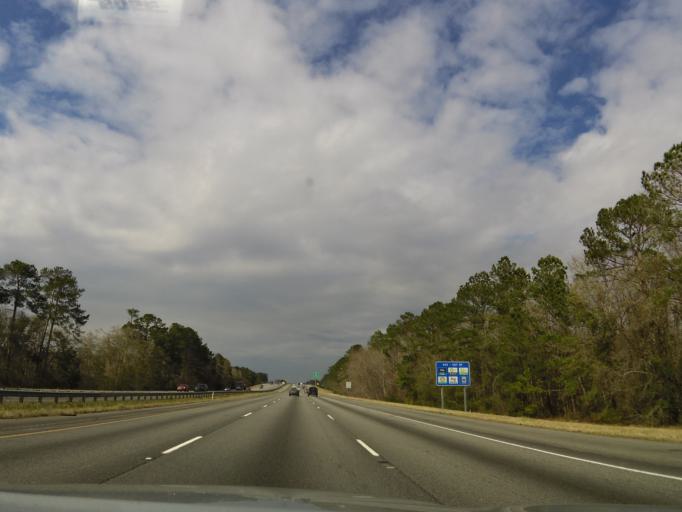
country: US
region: Georgia
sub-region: Bryan County
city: Richmond Hill
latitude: 31.9061
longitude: -81.3240
